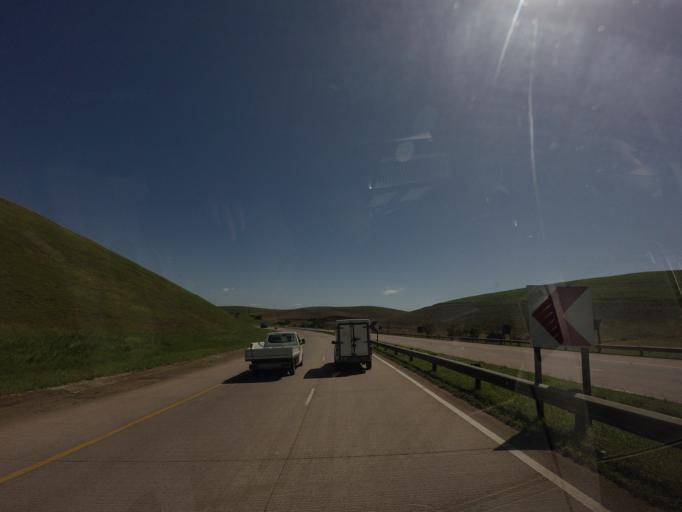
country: ZA
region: KwaZulu-Natal
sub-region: iLembe District Municipality
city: Stanger
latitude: -29.3889
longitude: 31.2963
